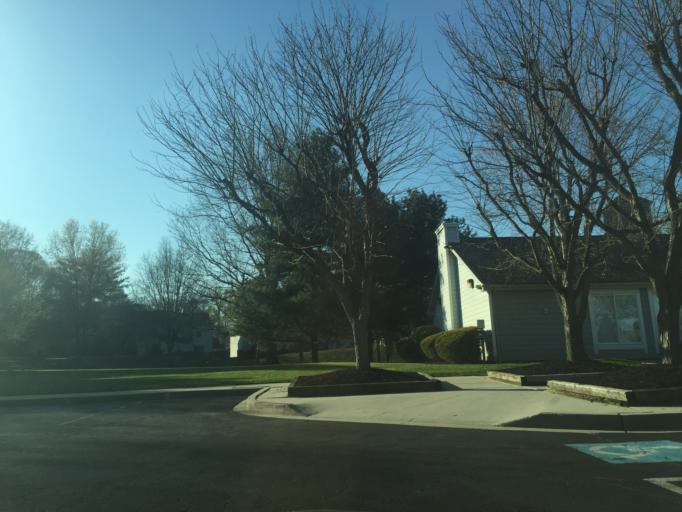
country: US
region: Maryland
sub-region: Harford County
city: Riverside
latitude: 39.4750
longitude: -76.2390
